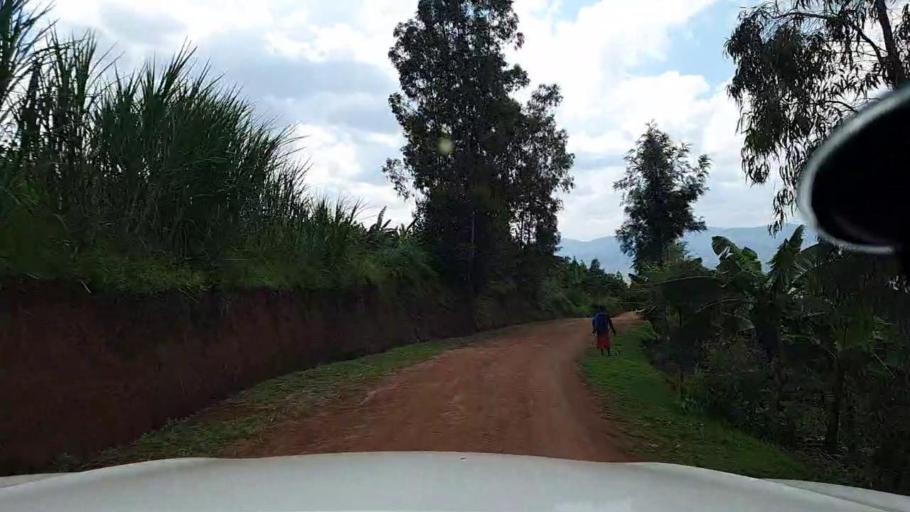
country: RW
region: Southern Province
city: Gitarama
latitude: -1.8385
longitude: 29.8283
